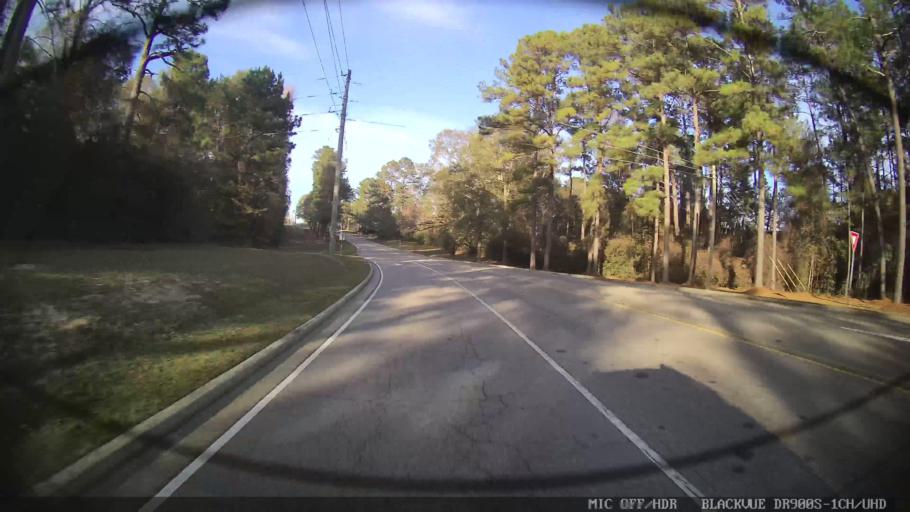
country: US
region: Mississippi
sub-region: Forrest County
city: Hattiesburg
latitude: 31.2324
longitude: -89.3027
